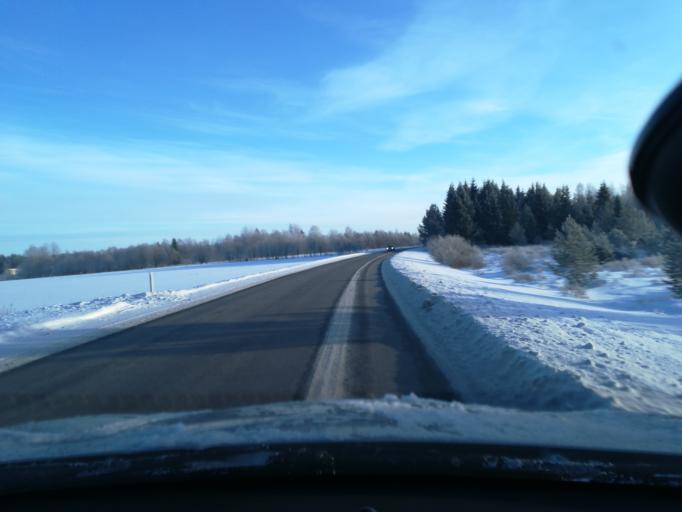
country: EE
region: Harju
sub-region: Keila linn
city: Keila
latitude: 59.3805
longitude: 24.4501
